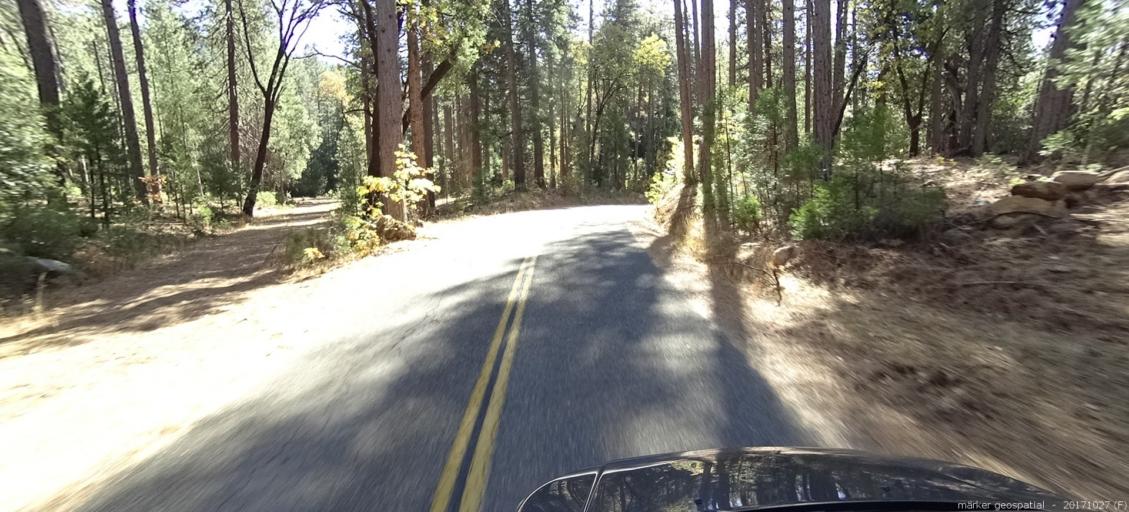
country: US
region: California
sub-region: Shasta County
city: Shingletown
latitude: 40.7352
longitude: -121.9573
